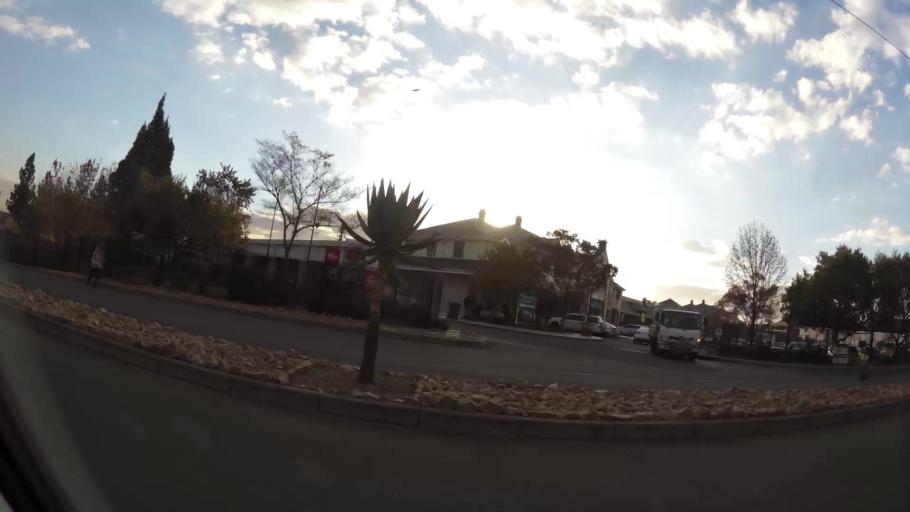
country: ZA
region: Gauteng
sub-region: City of Johannesburg Metropolitan Municipality
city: Diepsloot
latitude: -26.0021
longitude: 27.9836
